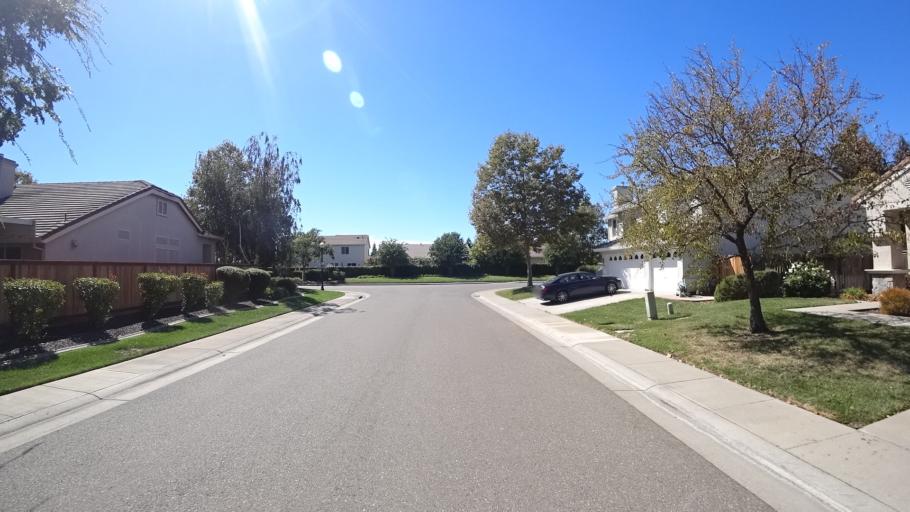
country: US
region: California
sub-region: Sacramento County
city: Laguna
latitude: 38.4132
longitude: -121.4665
